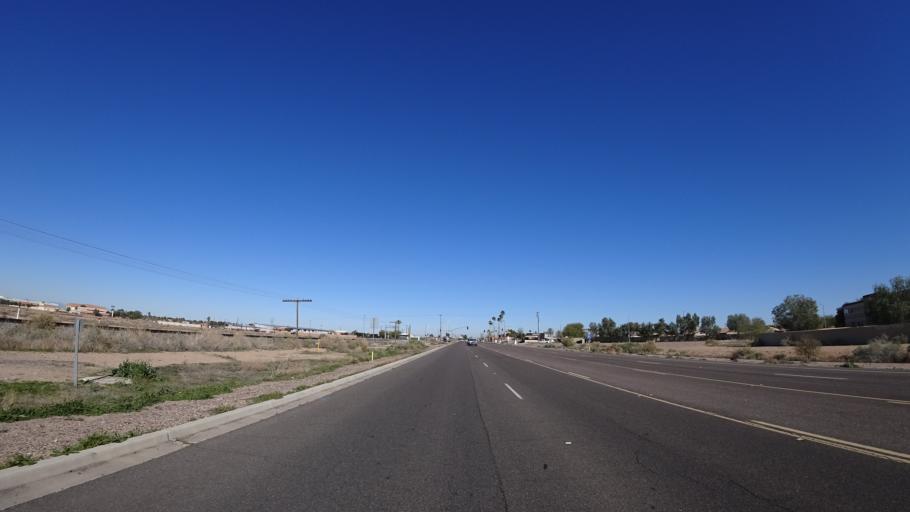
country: US
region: Arizona
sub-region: Maricopa County
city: Goodyear
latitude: 33.4240
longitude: -112.3594
